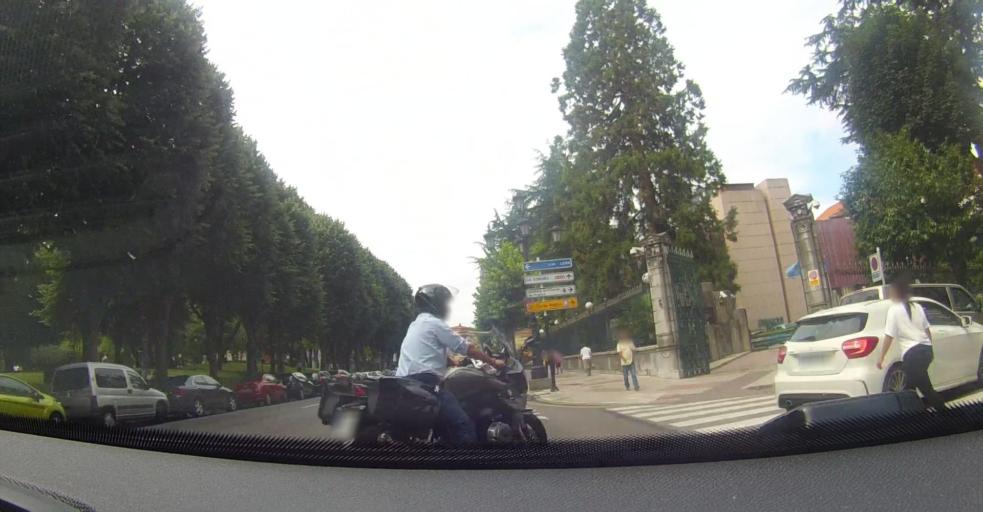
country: ES
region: Asturias
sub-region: Province of Asturias
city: Oviedo
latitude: 43.3627
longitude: -5.8517
